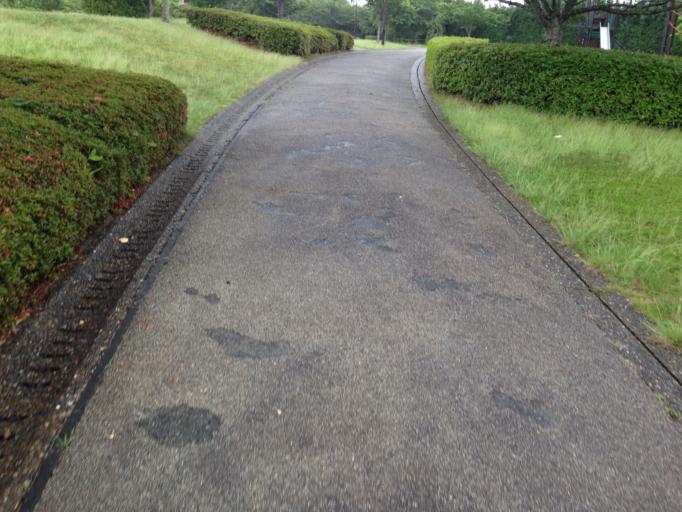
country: JP
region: Shizuoka
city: Fukuroi
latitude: 34.7443
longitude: 137.9413
